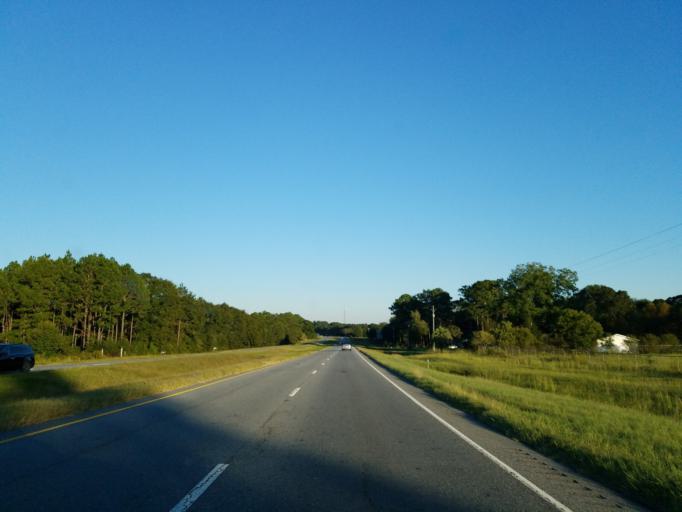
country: US
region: Georgia
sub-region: Tift County
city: Omega
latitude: 31.4773
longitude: -83.6760
